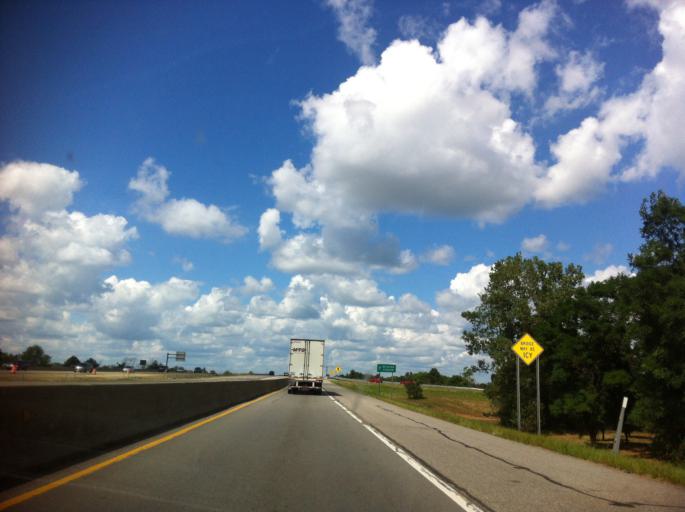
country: US
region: Michigan
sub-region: Washtenaw County
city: Ypsilanti
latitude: 42.2214
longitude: -83.6851
